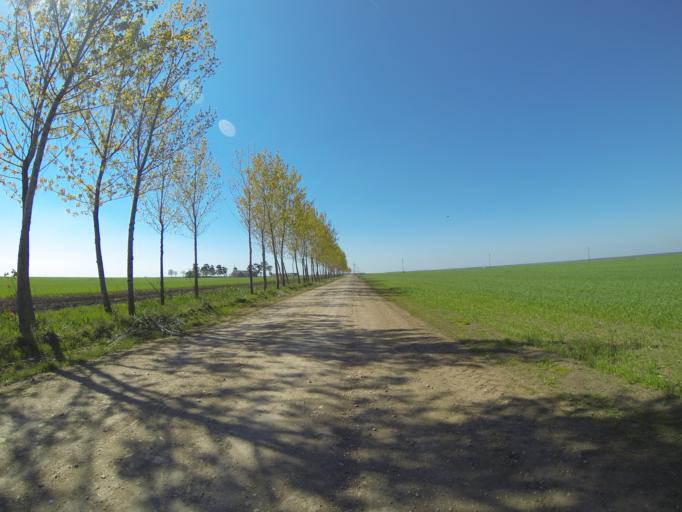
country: RO
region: Dolj
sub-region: Comuna Caloparu
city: Salcuta
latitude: 44.1441
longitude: 23.6983
